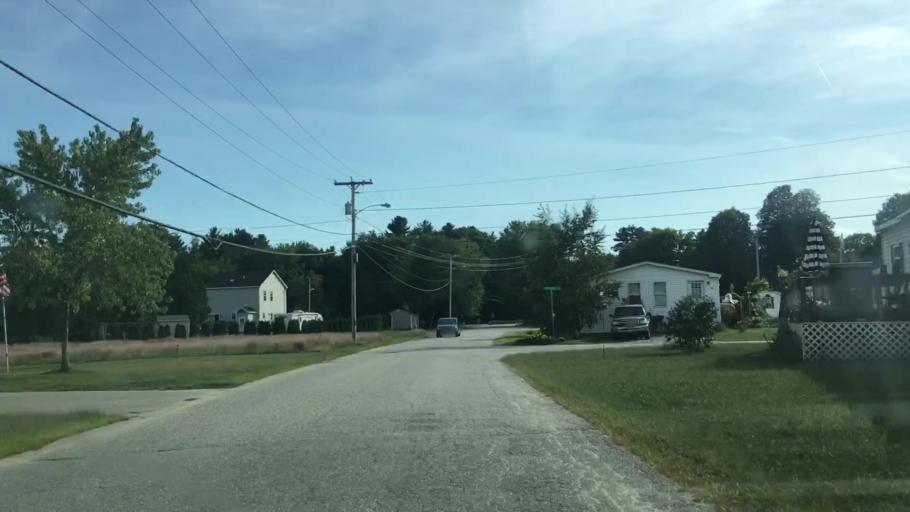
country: US
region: Maine
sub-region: Sagadahoc County
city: North Bath
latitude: 43.9346
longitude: -69.8744
